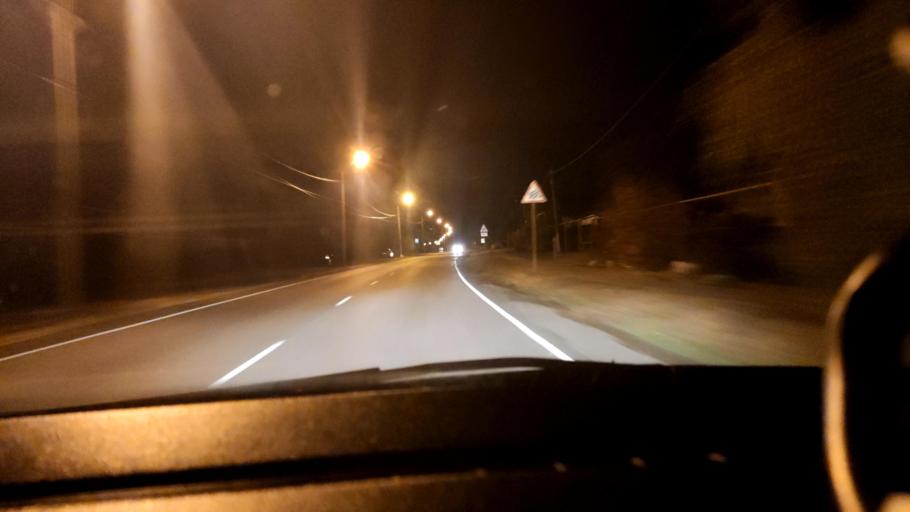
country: RU
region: Voronezj
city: Shilovo
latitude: 51.5561
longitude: 39.0629
